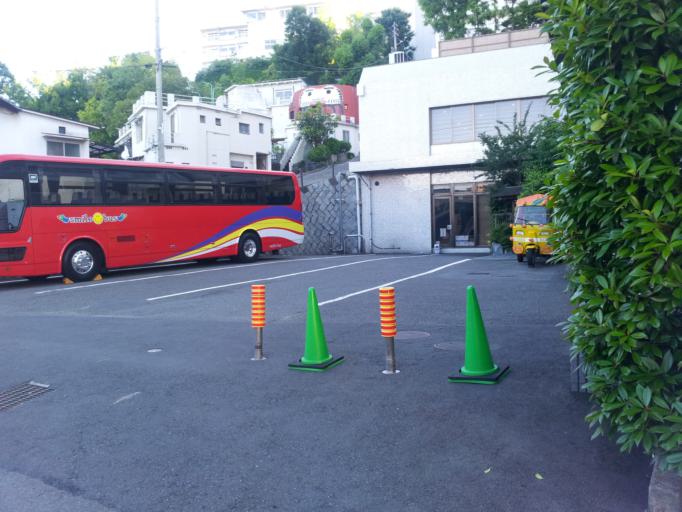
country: JP
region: Ehime
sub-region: Shikoku-chuo Shi
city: Matsuyama
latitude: 33.8479
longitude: 132.7904
